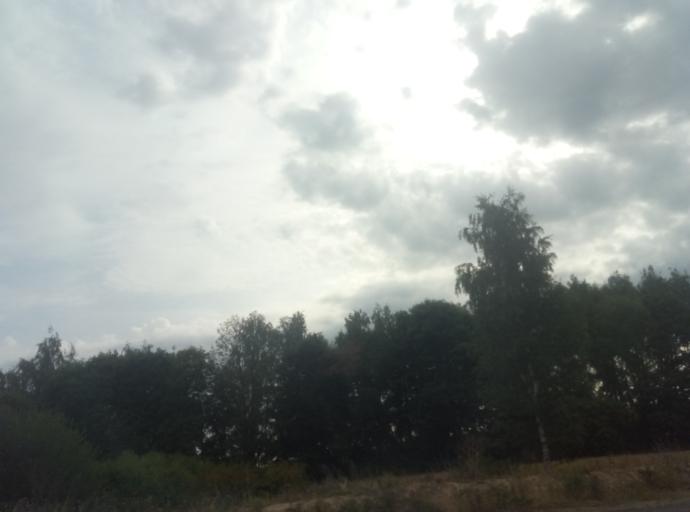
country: RU
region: Tula
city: Dubovka
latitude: 53.8821
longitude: 38.0626
